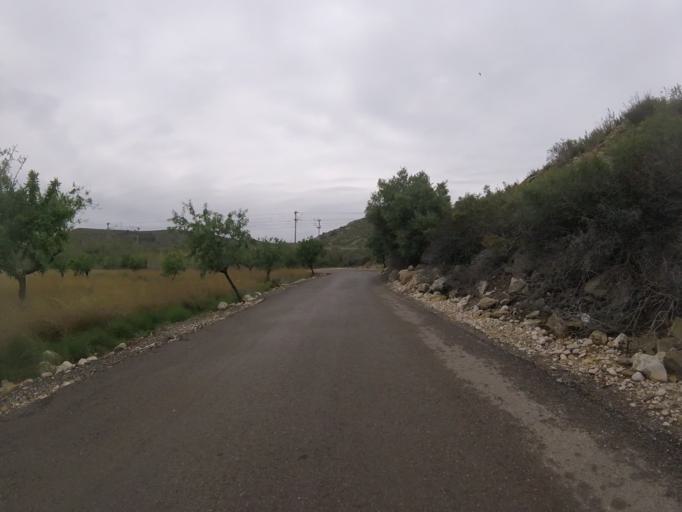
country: ES
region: Valencia
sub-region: Provincia de Castello
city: Alcala de Xivert
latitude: 40.2730
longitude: 0.2426
